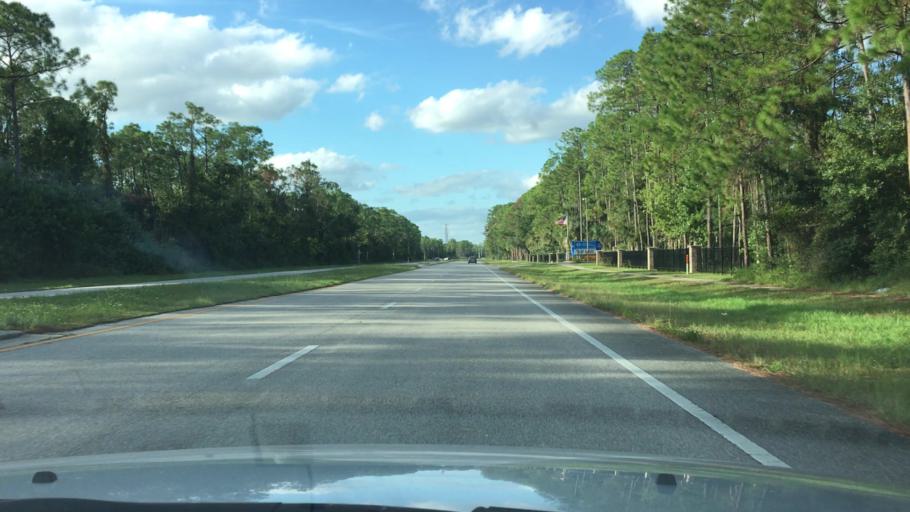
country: US
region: Florida
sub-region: Volusia County
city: Daytona Beach
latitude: 29.1923
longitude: -81.0832
